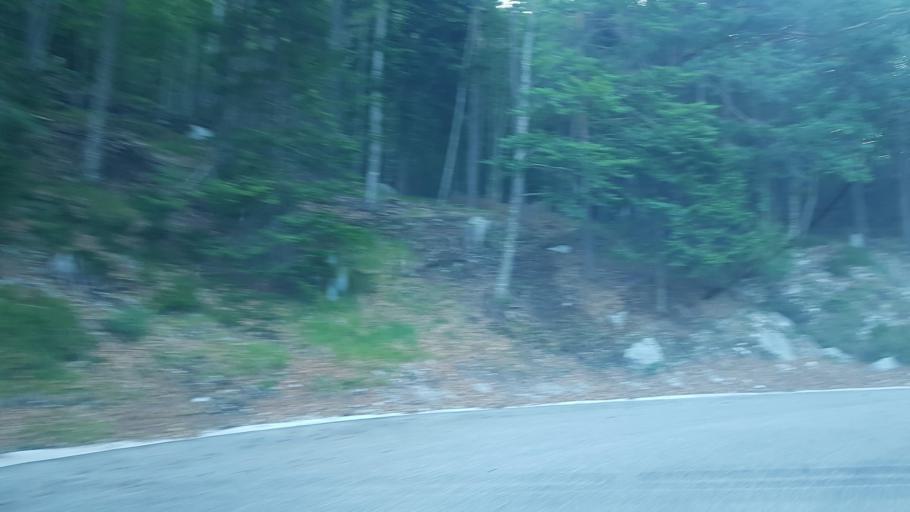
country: IT
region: Friuli Venezia Giulia
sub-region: Provincia di Udine
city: Malborghetto
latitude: 46.4619
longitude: 13.4232
